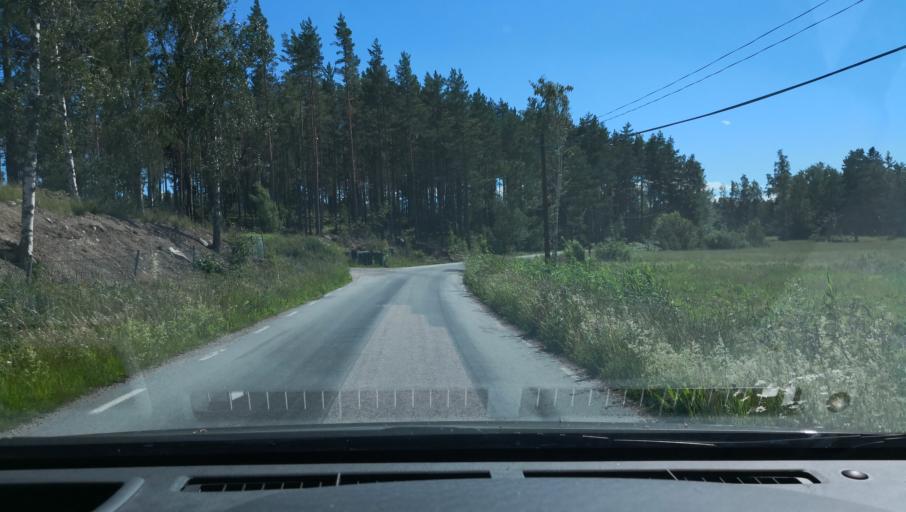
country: SE
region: Soedermanland
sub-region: Eskilstuna Kommun
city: Hallbybrunn
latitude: 59.3148
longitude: 16.3786
